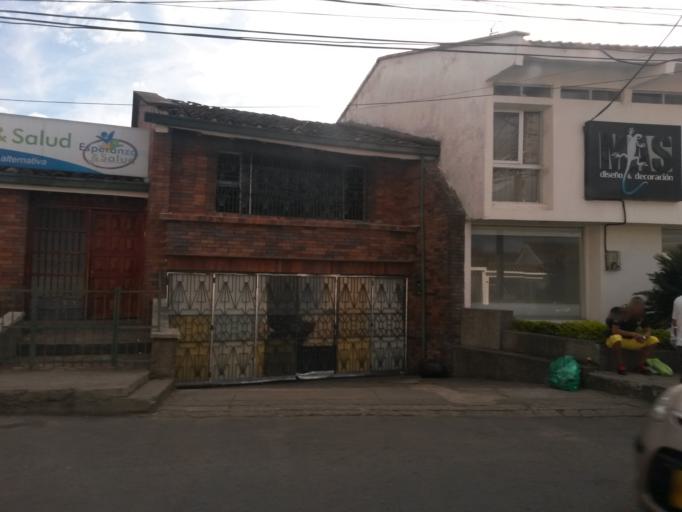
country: CO
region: Cauca
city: Popayan
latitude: 2.4569
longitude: -76.5975
